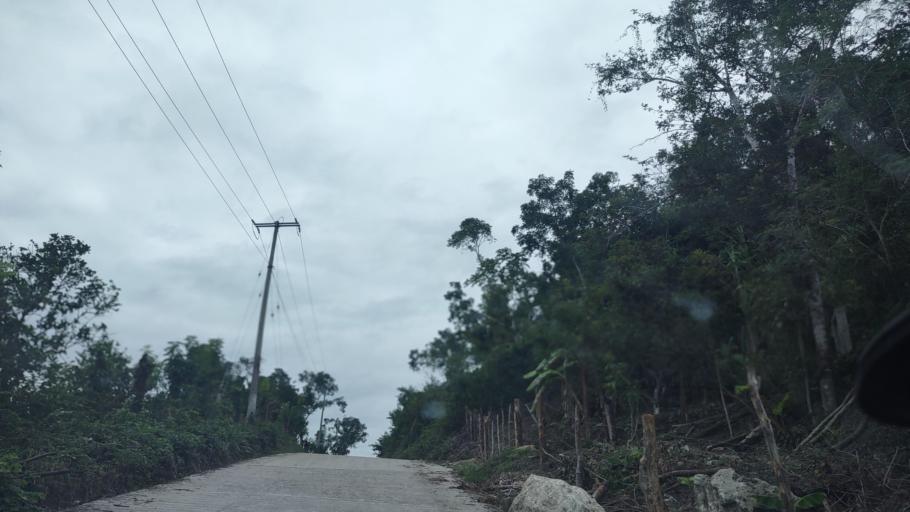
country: MX
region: Veracruz
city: Papantla de Olarte
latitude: 20.4371
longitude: -97.2735
